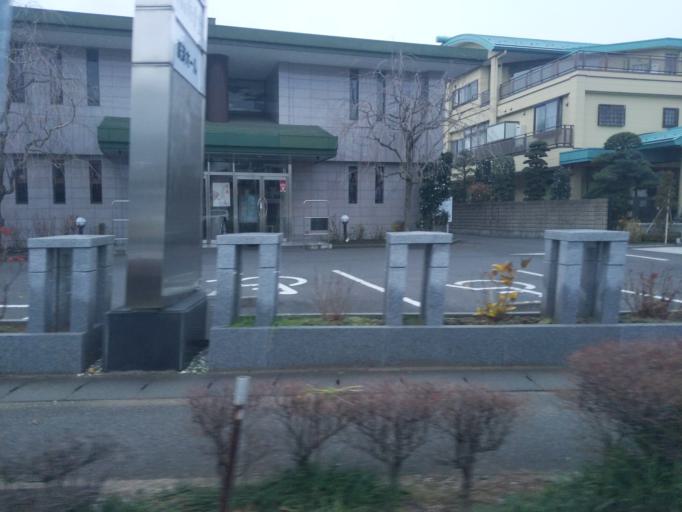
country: JP
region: Saitama
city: Koshigaya
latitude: 35.8608
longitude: 139.7960
